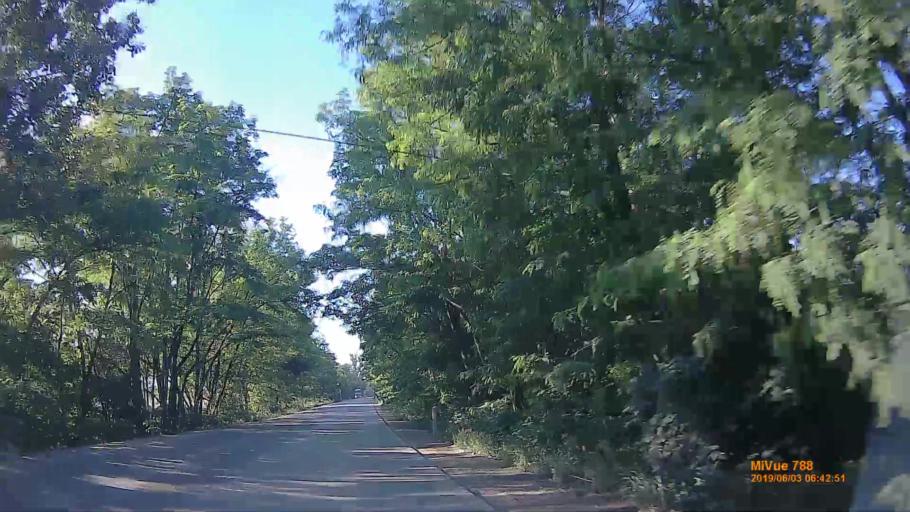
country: HU
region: Pest
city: Delegyhaza
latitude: 47.2618
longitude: 19.1196
